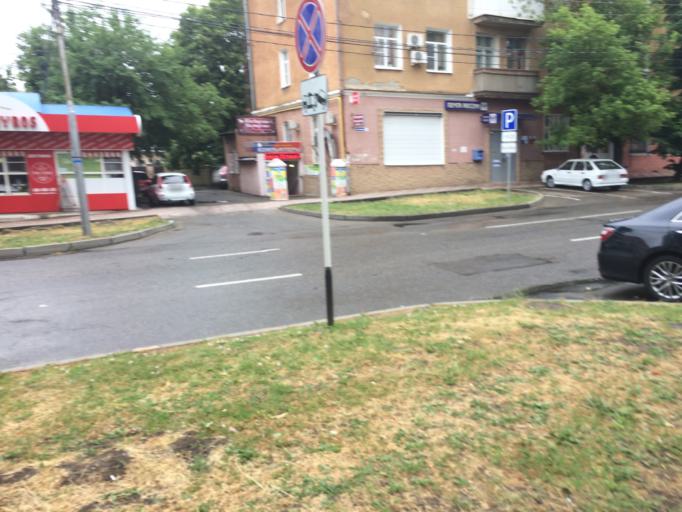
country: RU
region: Stavropol'skiy
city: Stavropol'
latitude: 45.0399
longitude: 41.9629
